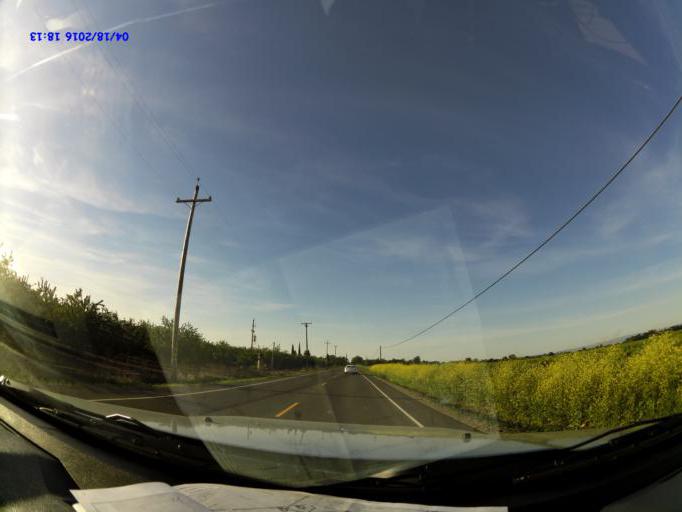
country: US
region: California
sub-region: San Joaquin County
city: Escalon
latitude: 37.9198
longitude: -121.0002
